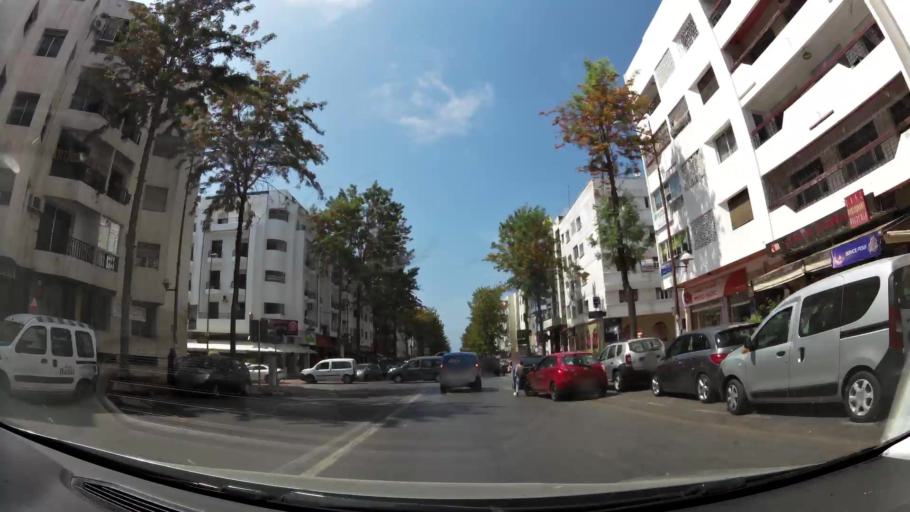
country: MA
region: Rabat-Sale-Zemmour-Zaer
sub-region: Rabat
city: Rabat
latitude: 33.9950
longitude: -6.8474
